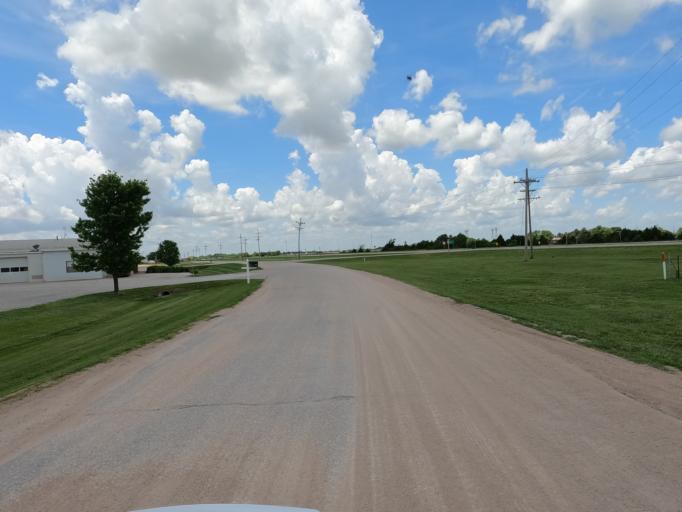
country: US
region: Kansas
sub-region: Reno County
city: South Hutchinson
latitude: 37.9991
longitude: -98.0273
